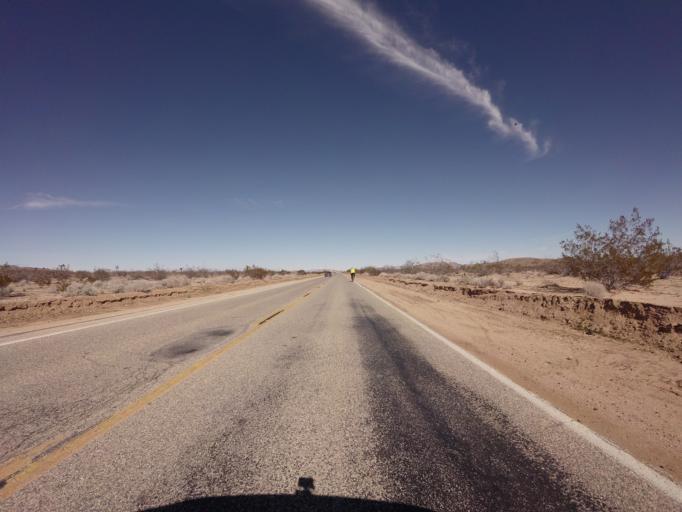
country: US
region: California
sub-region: San Bernardino County
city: Yucca Valley
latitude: 34.2396
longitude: -116.3933
